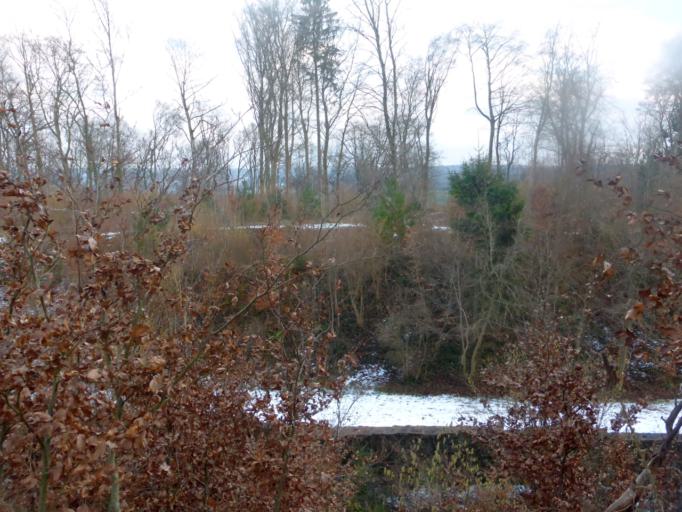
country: LU
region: Luxembourg
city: Belvaux
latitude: 49.5128
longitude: 5.9200
